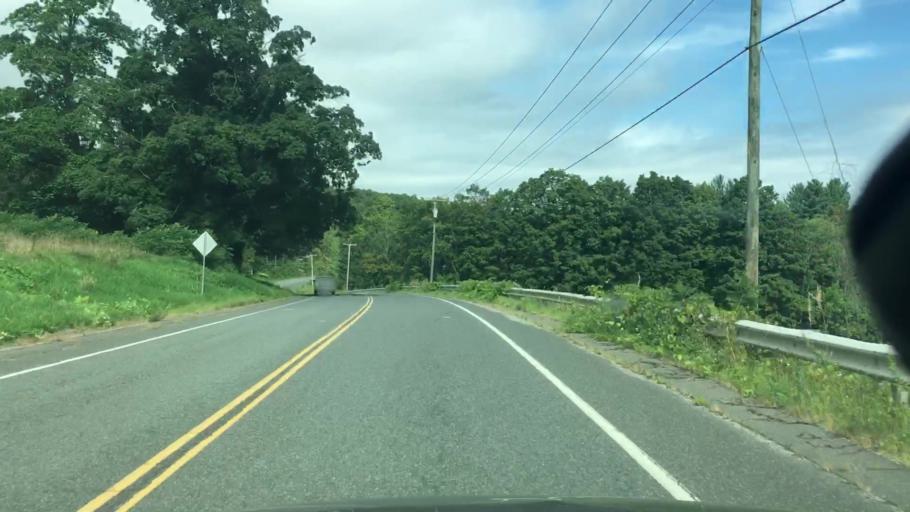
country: US
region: Massachusetts
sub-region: Franklin County
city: Colrain
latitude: 42.6573
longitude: -72.6786
